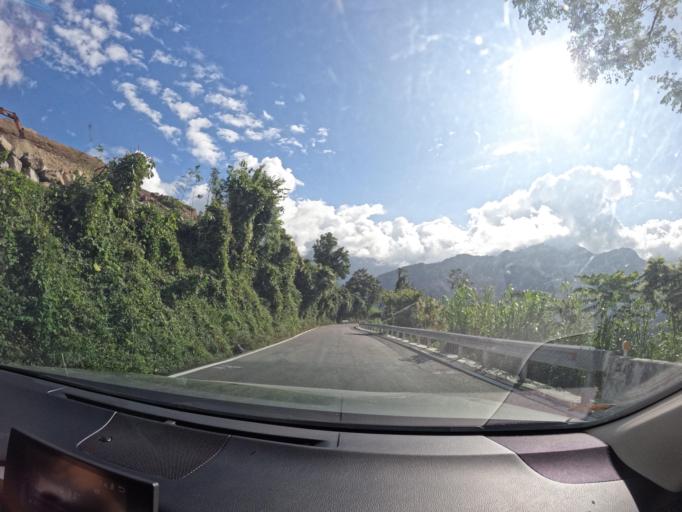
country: TW
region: Taiwan
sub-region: Taitung
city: Taitung
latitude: 23.1950
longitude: 121.0230
